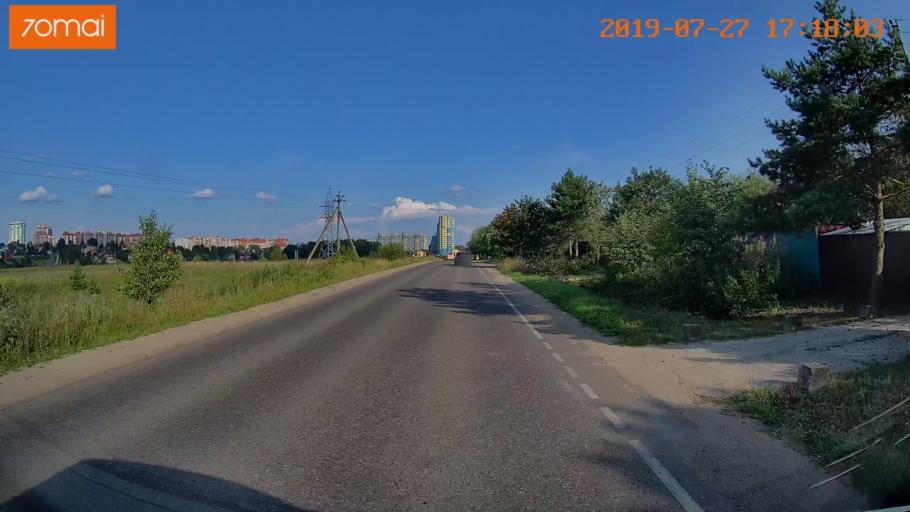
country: RU
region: Ivanovo
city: Novo-Talitsy
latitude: 57.0329
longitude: 40.9022
